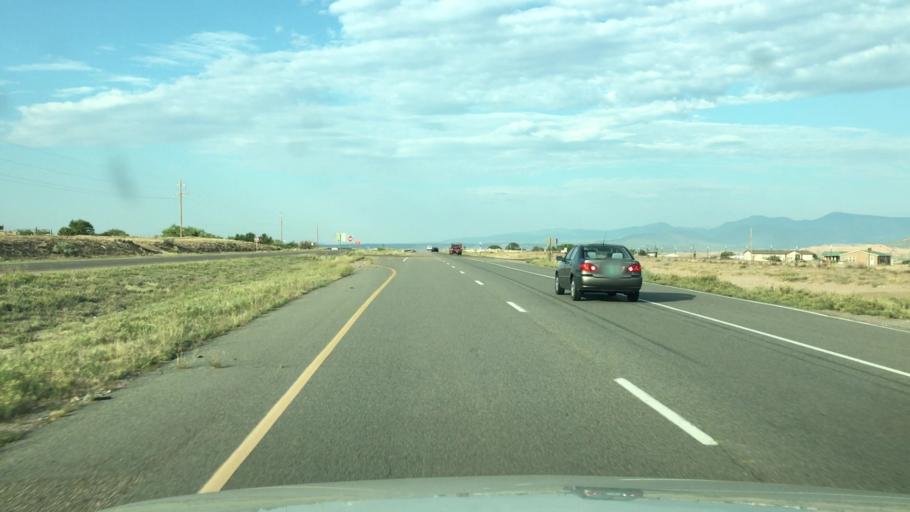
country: US
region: New Mexico
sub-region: Rio Arriba County
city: Ohkay Owingeh
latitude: 36.1188
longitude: -106.0168
